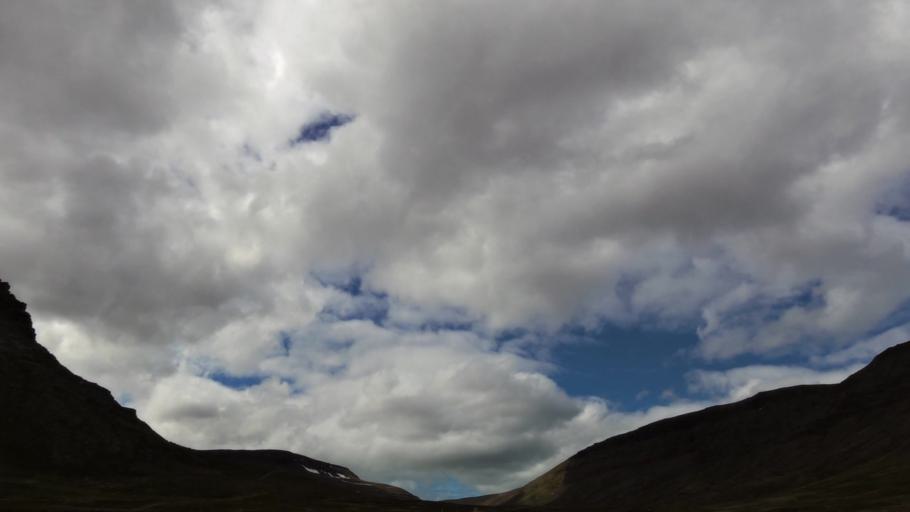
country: IS
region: Westfjords
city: Isafjoerdur
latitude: 66.1579
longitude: -23.2926
